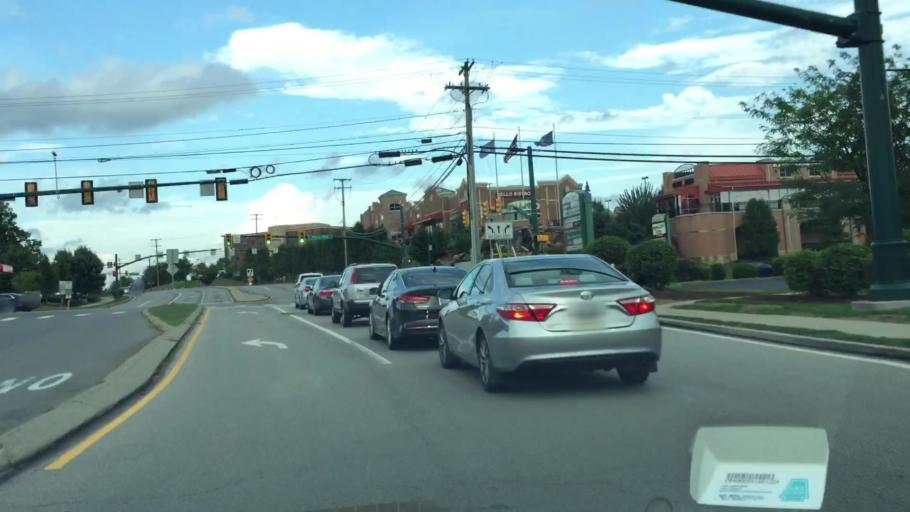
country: US
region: Pennsylvania
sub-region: Allegheny County
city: Bradford Woods
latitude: 40.6330
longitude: -80.0603
